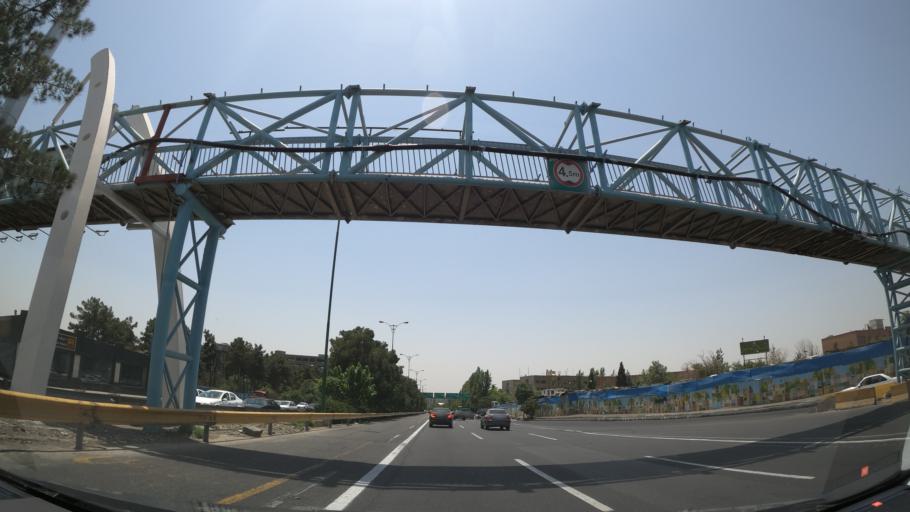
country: IR
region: Tehran
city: Tehran
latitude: 35.7247
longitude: 51.3811
